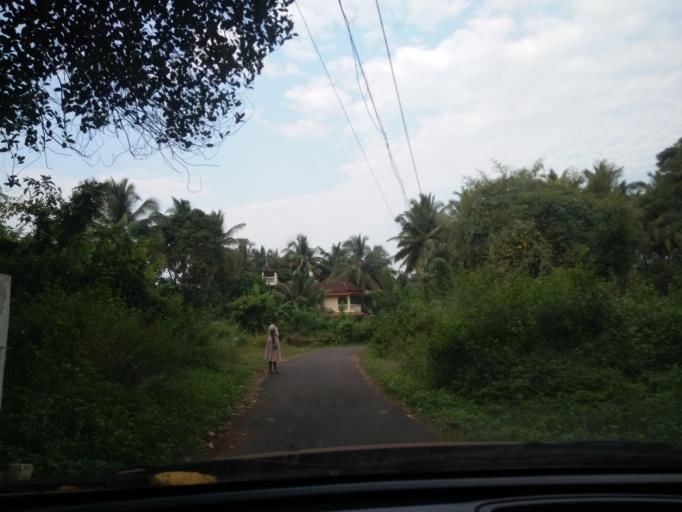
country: IN
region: Goa
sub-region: South Goa
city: Varca
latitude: 15.2275
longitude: 73.9540
